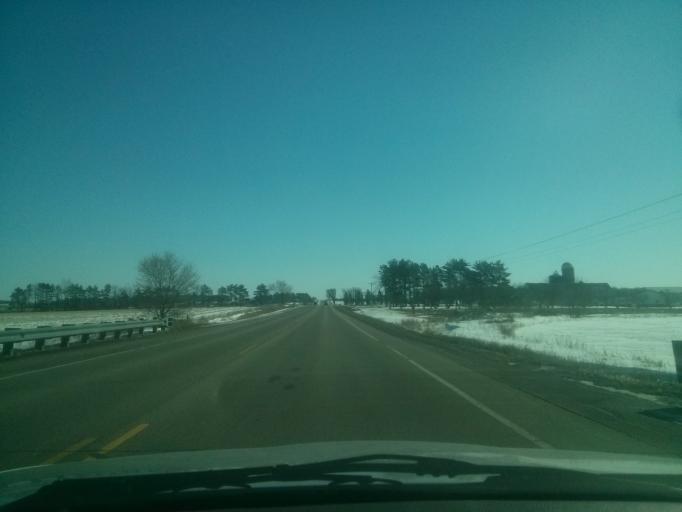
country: US
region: Wisconsin
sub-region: Saint Croix County
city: New Richmond
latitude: 45.1370
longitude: -92.4572
